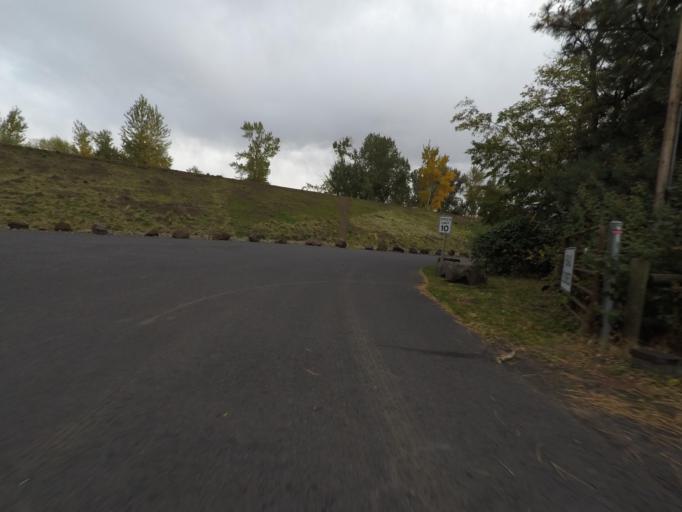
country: US
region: Washington
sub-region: Walla Walla County
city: Walla Walla East
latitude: 46.0825
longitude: -118.2525
